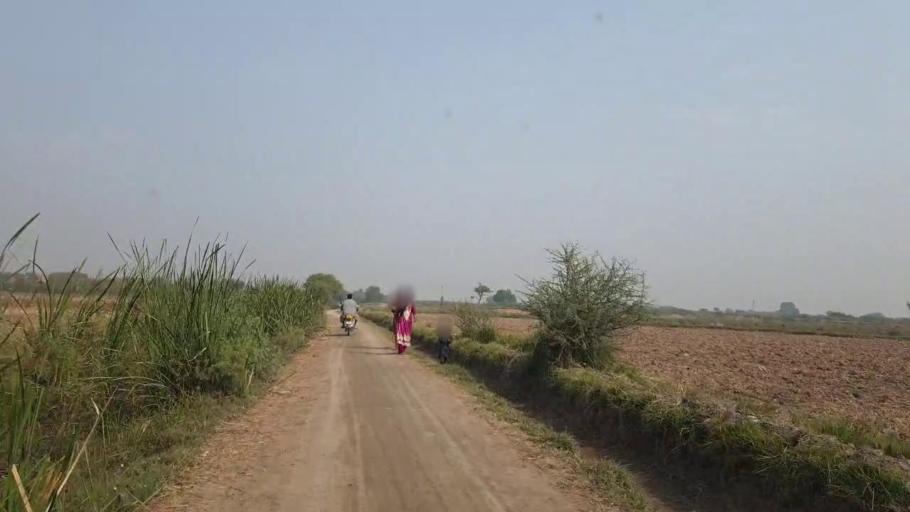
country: PK
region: Sindh
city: Matli
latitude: 25.0617
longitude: 68.6386
